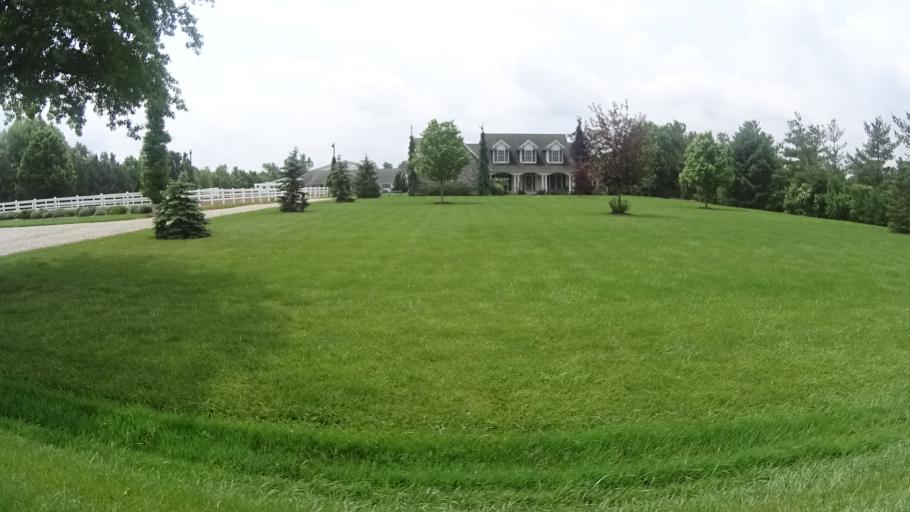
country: US
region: Ohio
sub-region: Huron County
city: Bellevue
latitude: 41.3260
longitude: -82.8218
